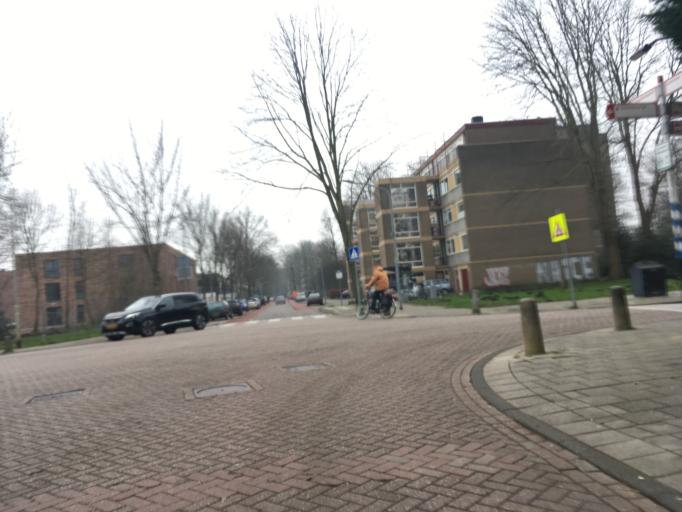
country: NL
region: North Holland
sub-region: Gemeente Haarlem
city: Haarlem
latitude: 52.3648
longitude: 4.6436
